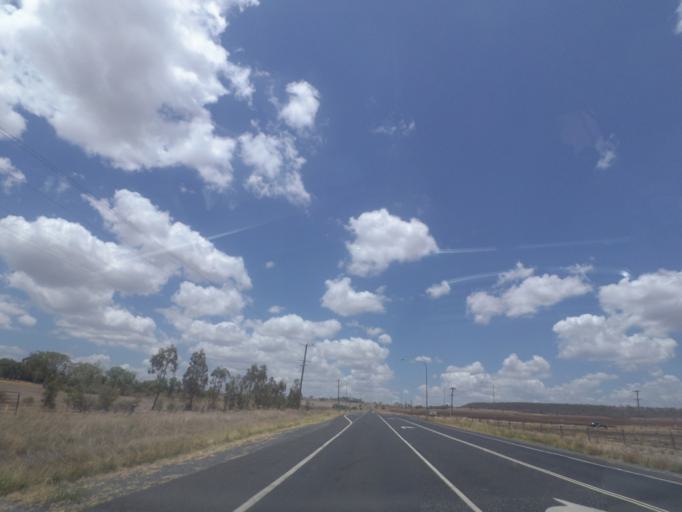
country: AU
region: Queensland
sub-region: Toowoomba
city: Top Camp
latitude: -27.7164
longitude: 151.9115
